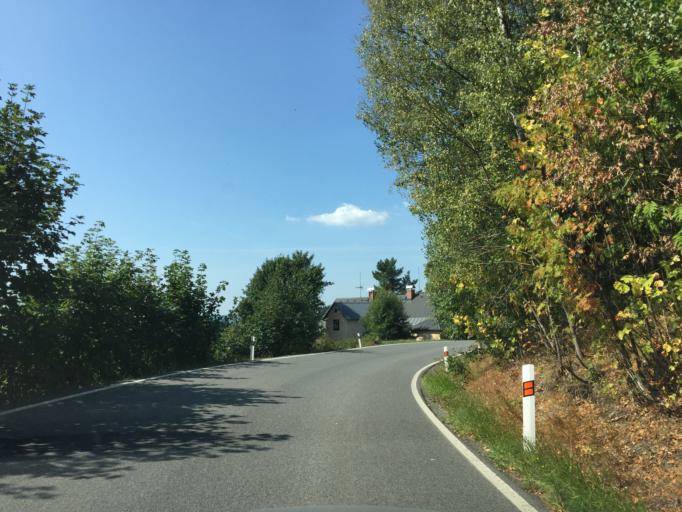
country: CZ
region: Liberecky
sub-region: Okres Jablonec nad Nisou
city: Janov nad Nisou
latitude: 50.7843
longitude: 15.1731
